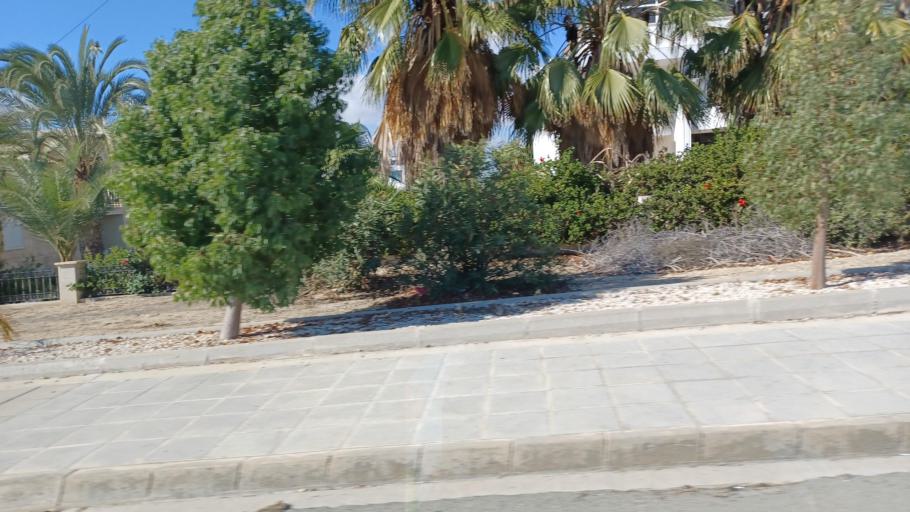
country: CY
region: Larnaka
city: Pyla
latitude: 34.9930
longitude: 33.6830
